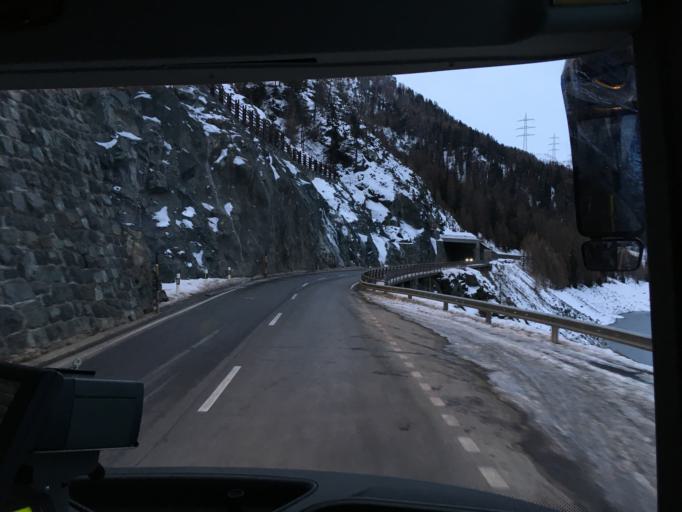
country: CH
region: Grisons
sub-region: Albula District
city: Tiefencastel
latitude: 46.5081
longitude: 9.6372
